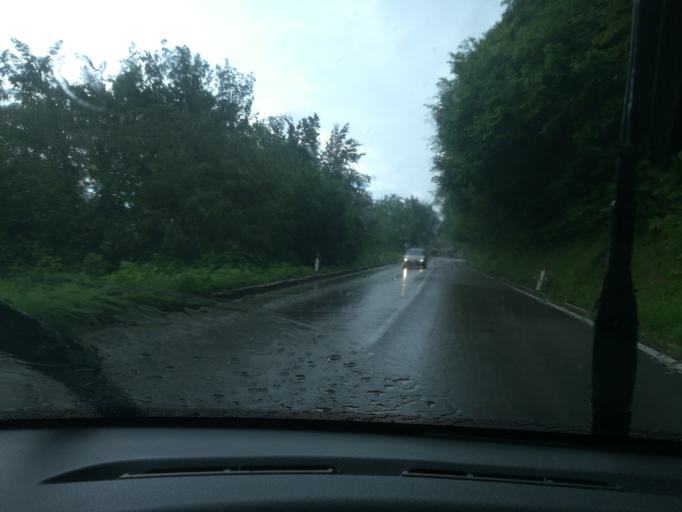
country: IT
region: The Marches
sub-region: Provincia di Macerata
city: Sarnano
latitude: 43.0396
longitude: 13.2914
